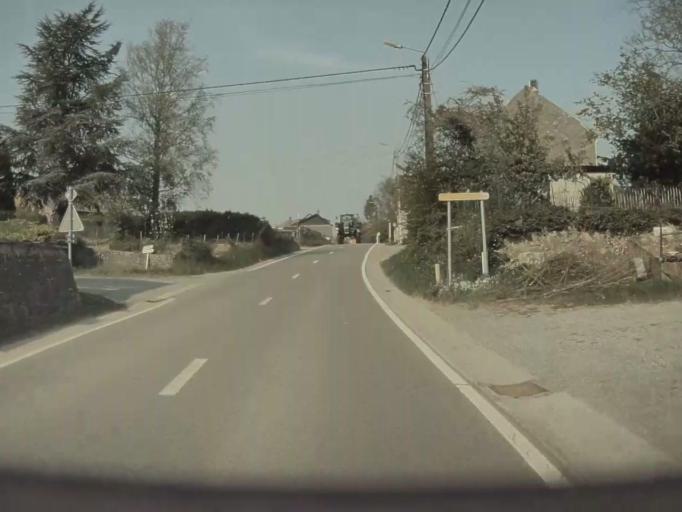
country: BE
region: Wallonia
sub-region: Province de Namur
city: Havelange
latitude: 50.3409
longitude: 5.2935
